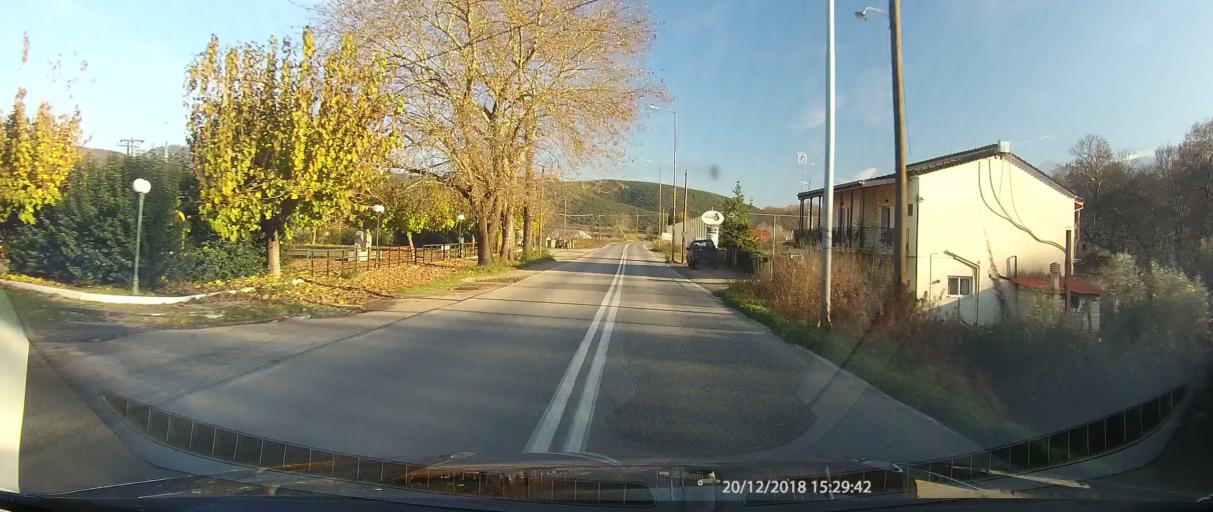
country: GR
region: Central Greece
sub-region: Nomos Fthiotidos
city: Lianokladhion
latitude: 38.9432
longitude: 22.2139
